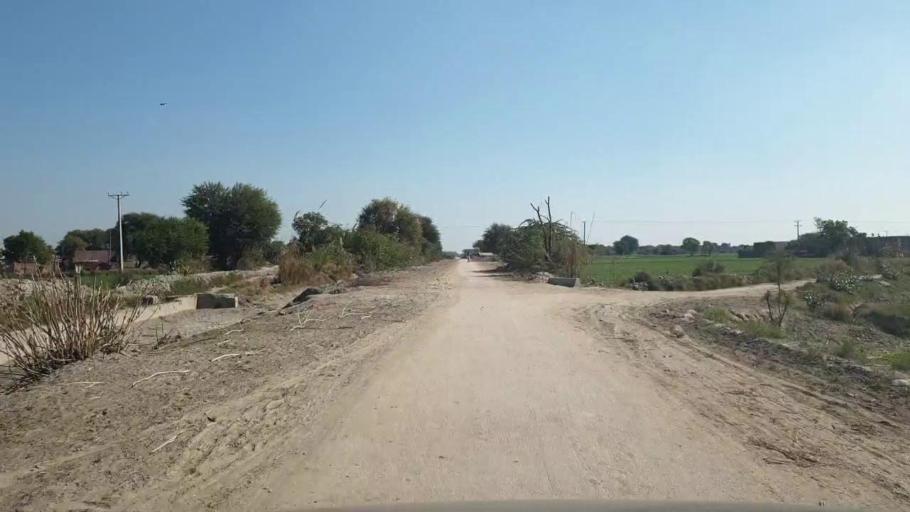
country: PK
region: Sindh
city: Shahpur Chakar
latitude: 26.1362
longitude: 68.6628
